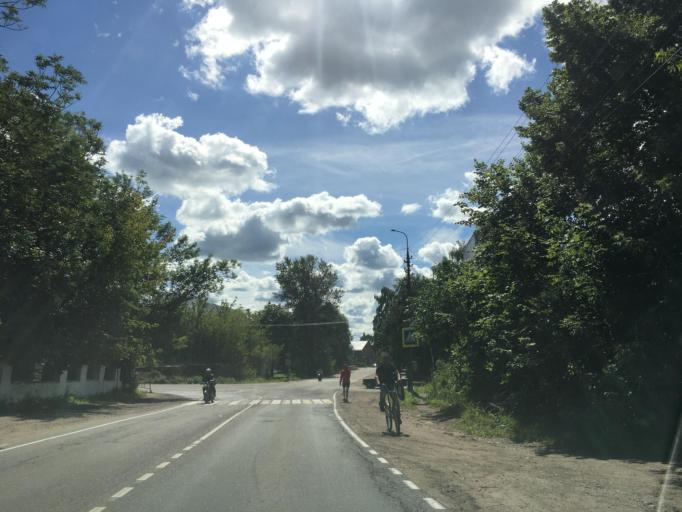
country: RU
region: Pskov
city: Ostrov
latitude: 57.3457
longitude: 28.3448
